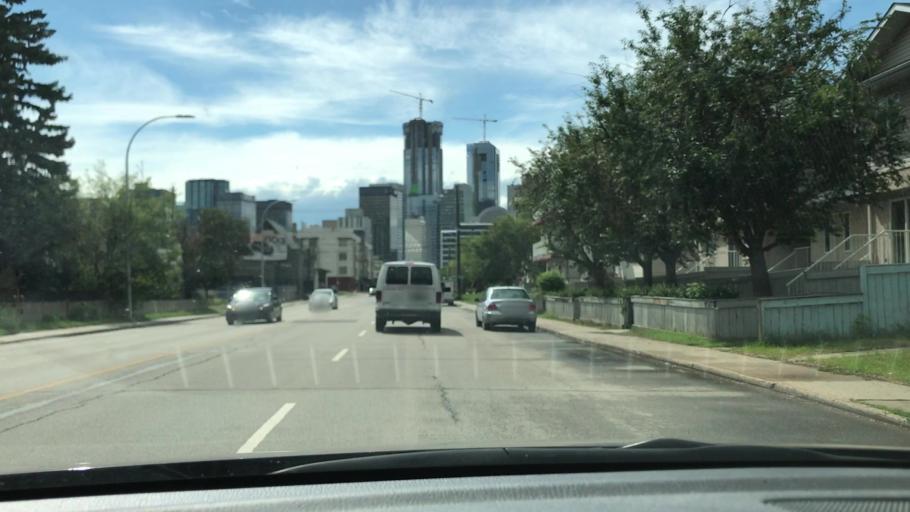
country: CA
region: Alberta
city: Edmonton
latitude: 53.5483
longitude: -113.4780
